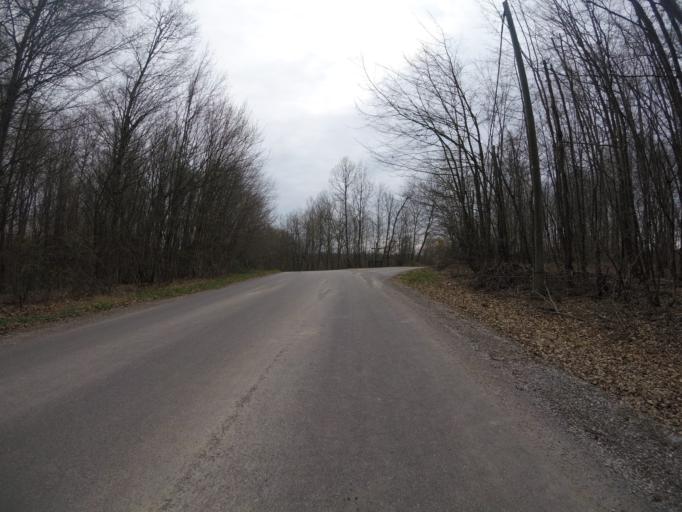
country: HR
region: Grad Zagreb
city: Strmec
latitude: 45.5978
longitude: 15.9113
